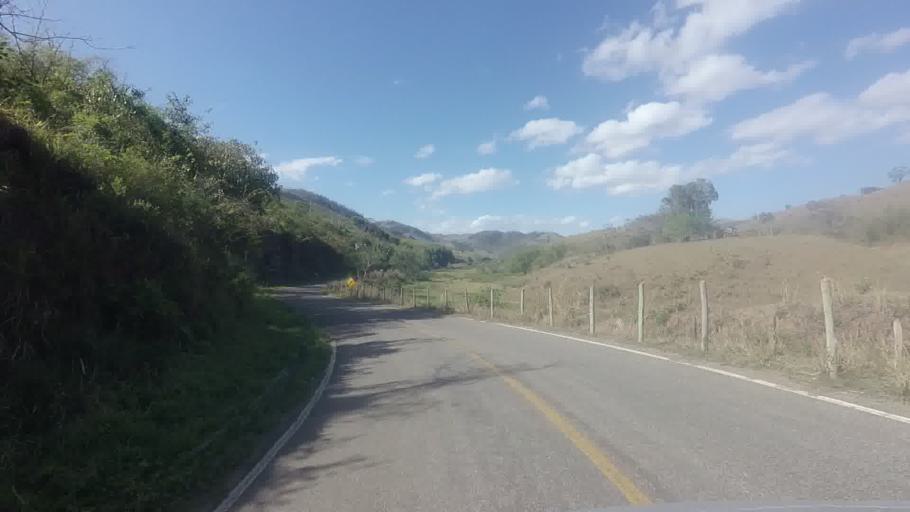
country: BR
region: Rio de Janeiro
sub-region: Bom Jesus Do Itabapoana
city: Bom Jesus do Itabapoana
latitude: -21.0981
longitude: -41.6360
